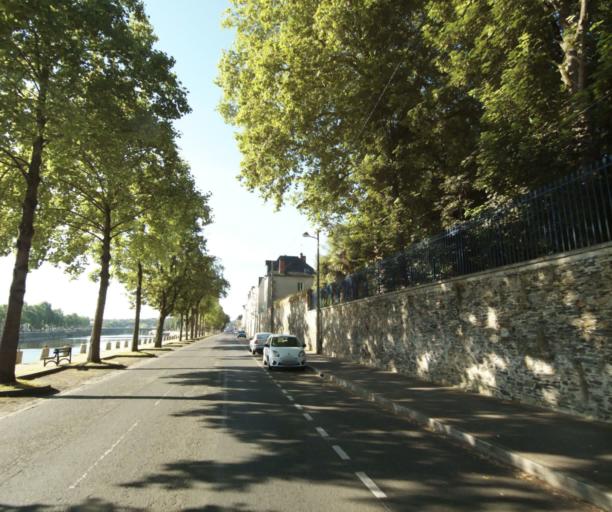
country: FR
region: Pays de la Loire
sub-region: Departement de la Mayenne
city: Laval
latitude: 48.0634
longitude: -0.7662
